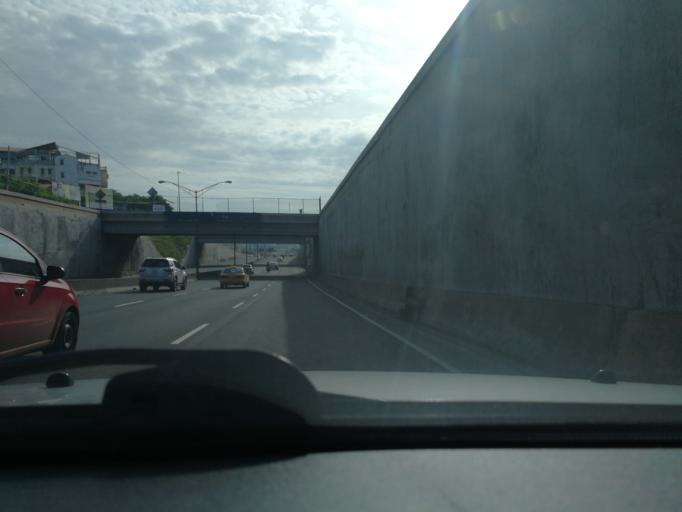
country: PA
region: Panama
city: San Miguelito
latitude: 9.0306
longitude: -79.4913
